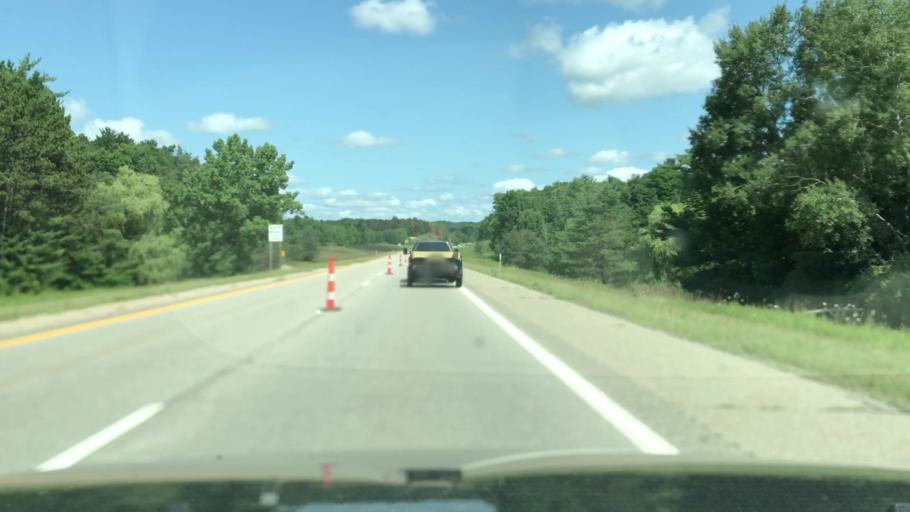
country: US
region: Michigan
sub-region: Mecosta County
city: Big Rapids
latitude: 43.7592
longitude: -85.5311
